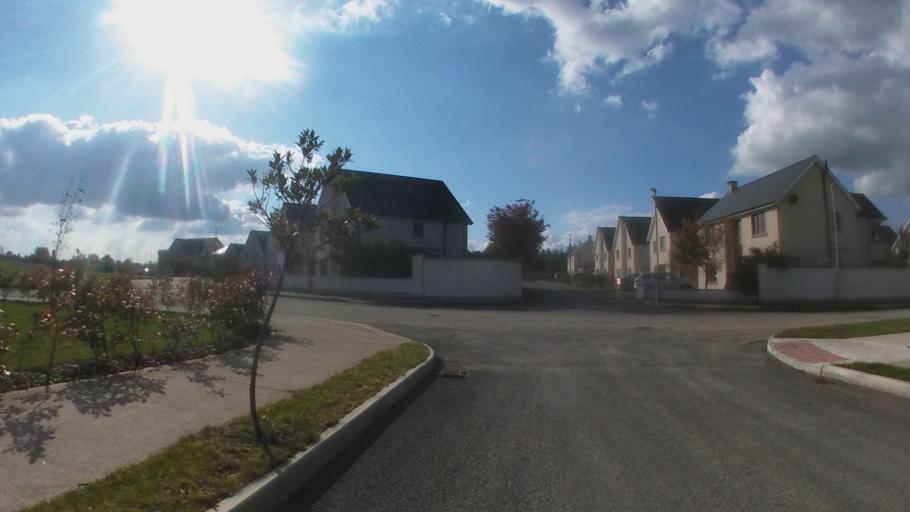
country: IE
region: Leinster
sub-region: Kilkenny
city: Kilkenny
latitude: 52.6715
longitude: -7.2329
